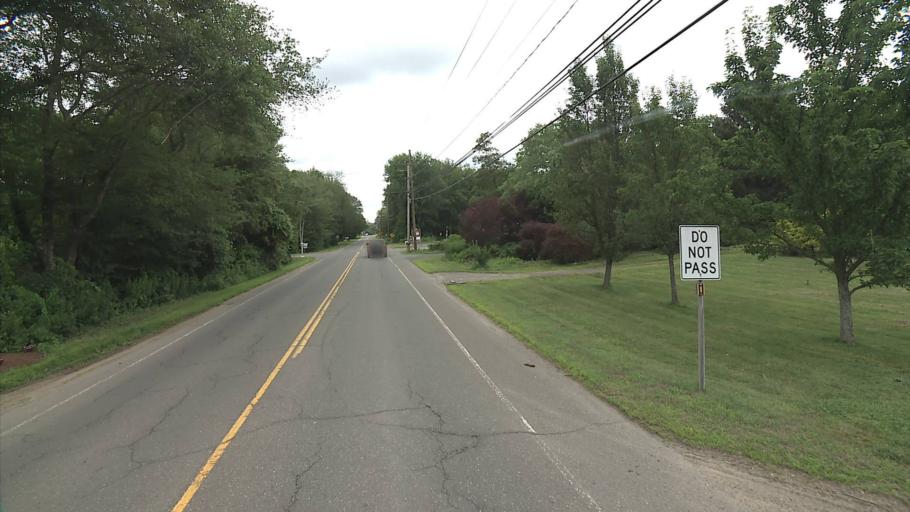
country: US
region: Connecticut
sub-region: Middlesex County
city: Clinton
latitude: 41.3572
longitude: -72.5556
